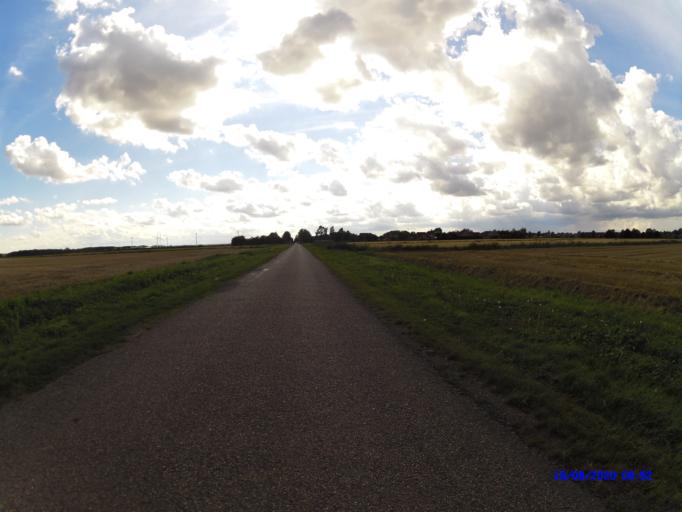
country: GB
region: England
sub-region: Cambridgeshire
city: Ramsey
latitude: 52.4833
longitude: -0.1005
